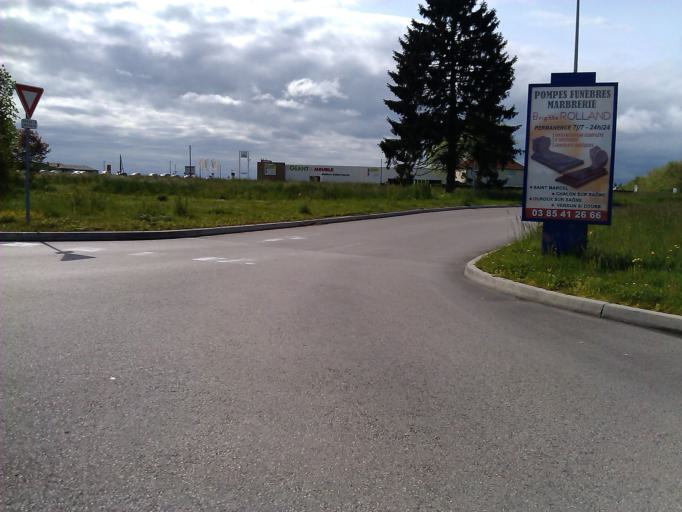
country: FR
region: Bourgogne
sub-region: Departement de Saone-et-Loire
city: Sevrey
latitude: 46.7493
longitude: 4.8480
